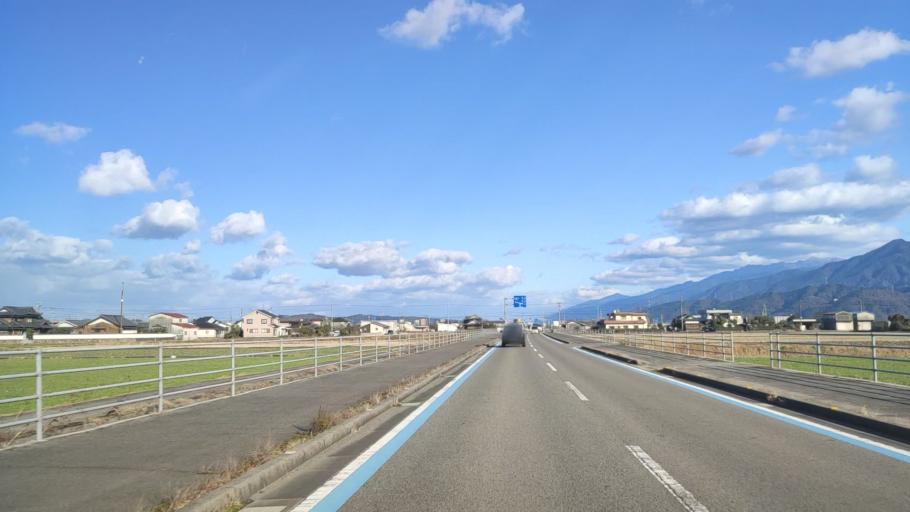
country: JP
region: Ehime
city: Saijo
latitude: 33.9083
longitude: 133.1521
